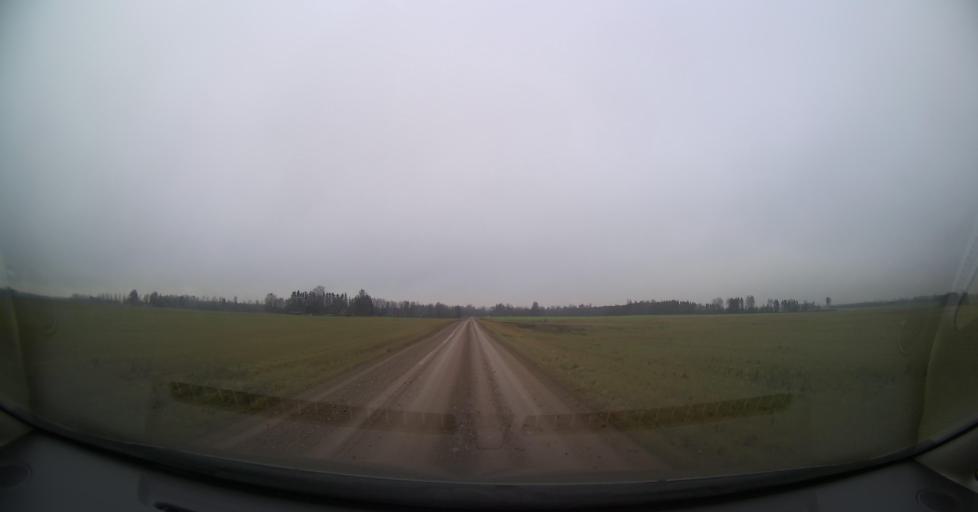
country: EE
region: Tartu
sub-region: Tartu linn
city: Tartu
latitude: 58.3864
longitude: 26.9275
